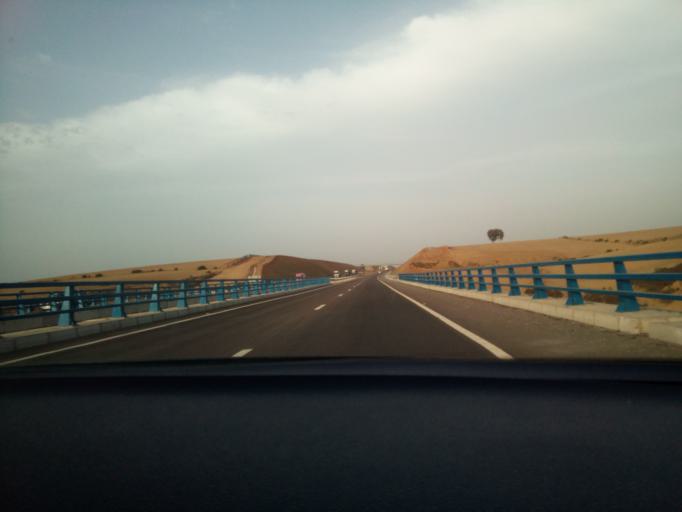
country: MA
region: Rabat-Sale-Zemmour-Zaer
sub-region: Skhirate-Temara
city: Temara
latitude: 33.8558
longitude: -6.8227
